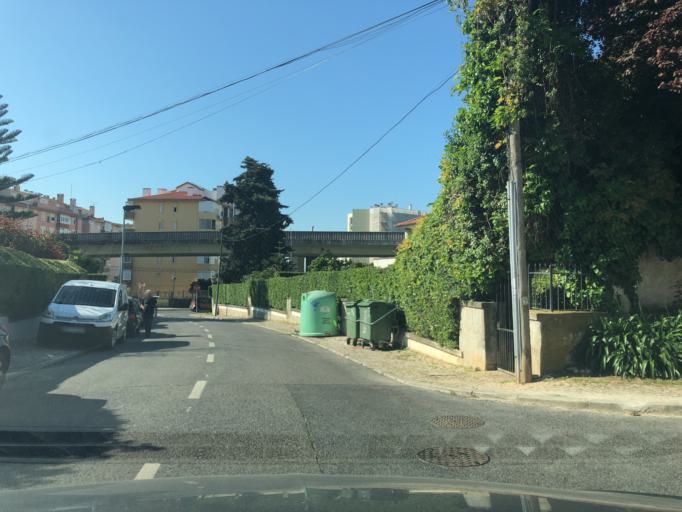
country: PT
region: Lisbon
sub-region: Oeiras
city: Paco de Arcos
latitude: 38.6946
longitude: -9.2991
